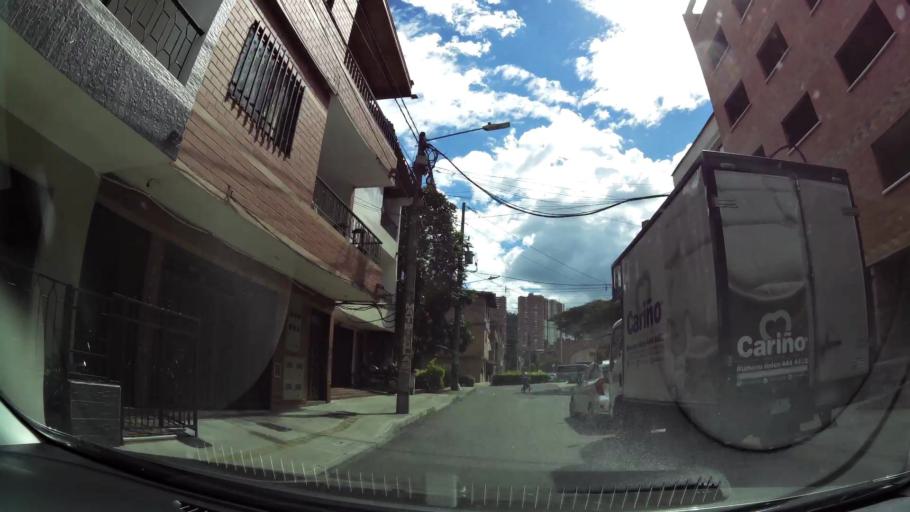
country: CO
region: Antioquia
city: Sabaneta
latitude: 6.1508
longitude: -75.6226
